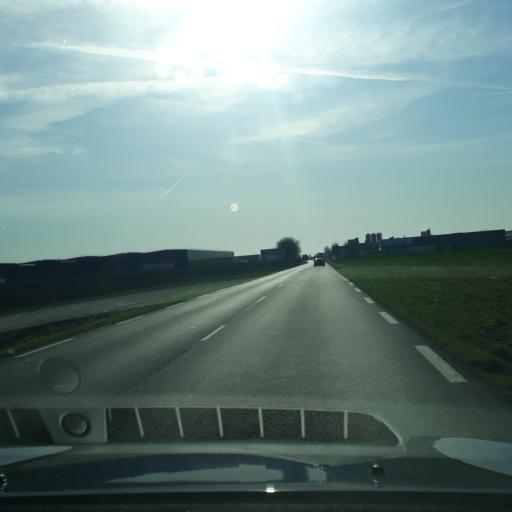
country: FR
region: Ile-de-France
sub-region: Departement de l'Essonne
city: Corbreuse
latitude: 48.4544
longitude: 1.9187
